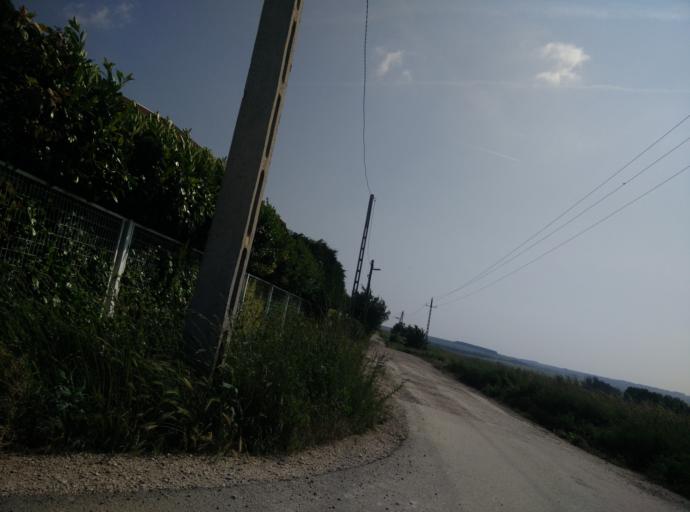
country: HU
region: Pest
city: Biatorbagy
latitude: 47.4744
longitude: 18.8081
